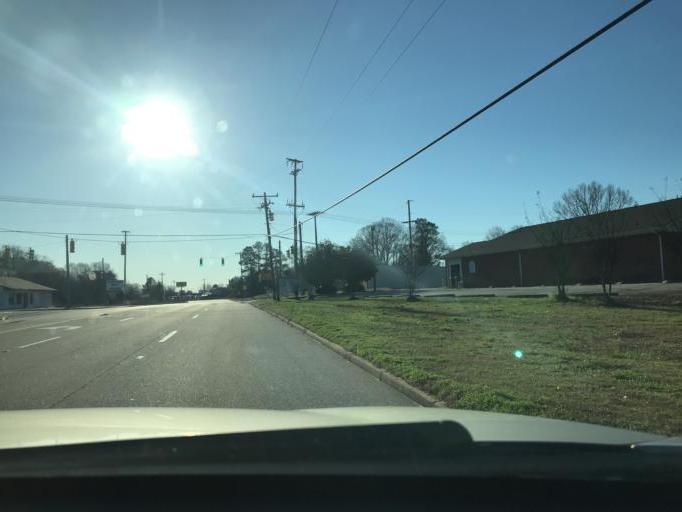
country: US
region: South Carolina
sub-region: Laurens County
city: Clinton
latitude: 34.4711
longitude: -81.9121
